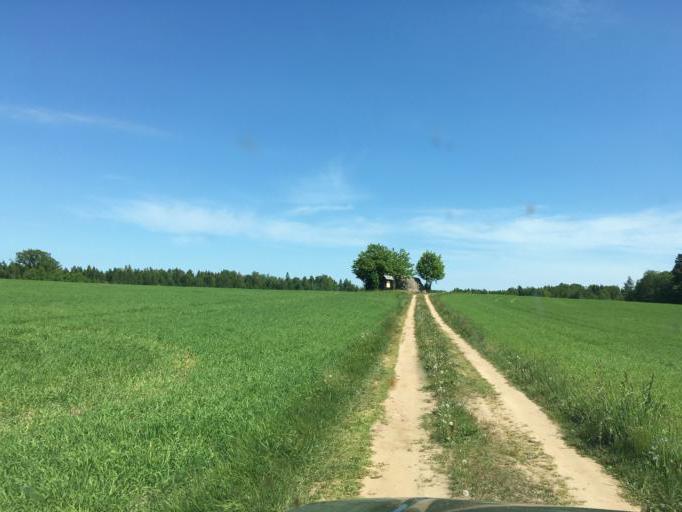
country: LV
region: Talsu Rajons
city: Valdemarpils
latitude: 57.3496
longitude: 22.7217
